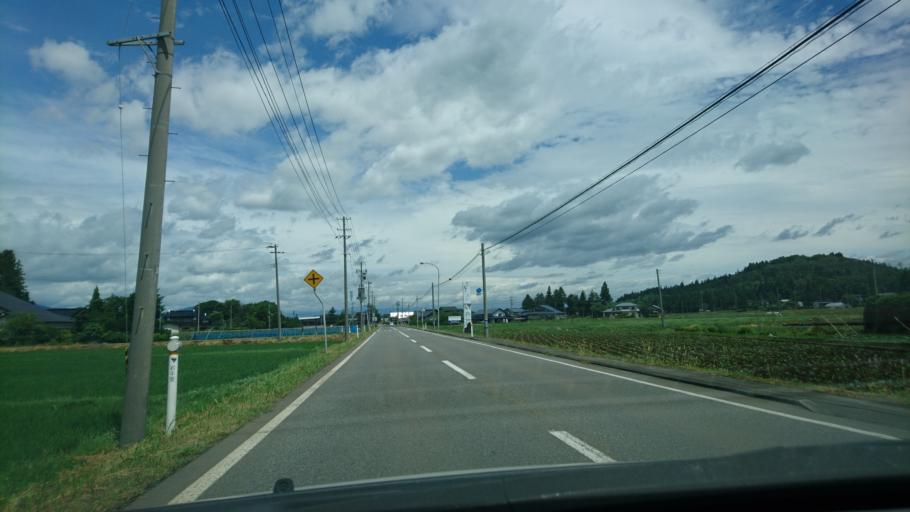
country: JP
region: Iwate
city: Hanamaki
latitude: 39.5312
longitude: 141.1891
